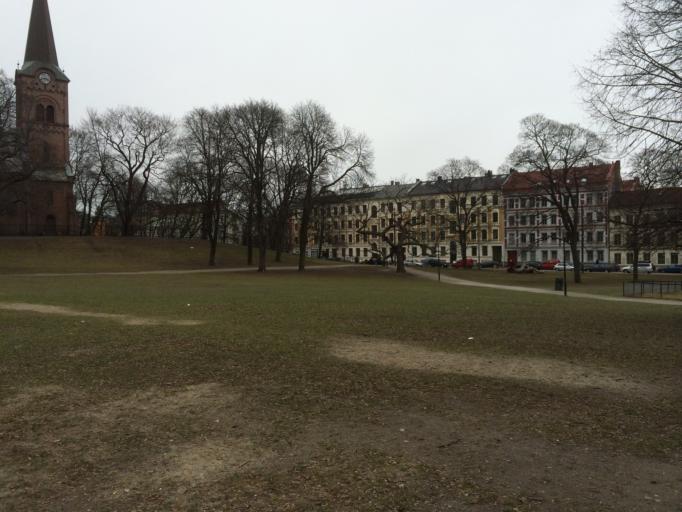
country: NO
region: Oslo
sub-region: Oslo
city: Oslo
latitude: 59.9230
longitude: 10.7644
